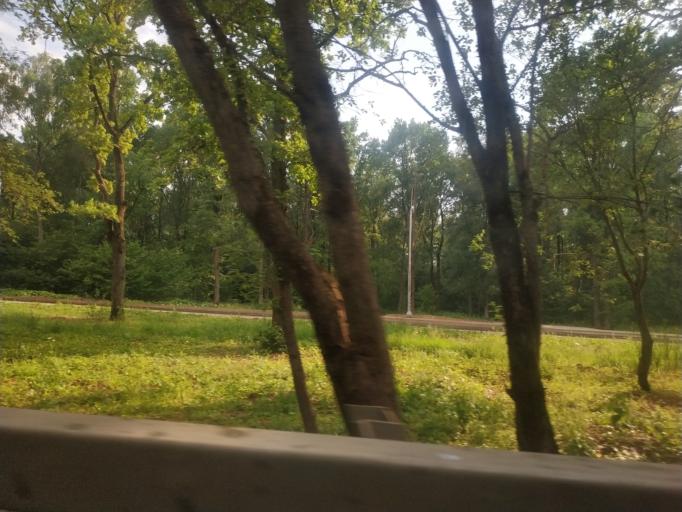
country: RU
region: Moskovskaya
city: Kommunarka
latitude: 55.5846
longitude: 37.4604
